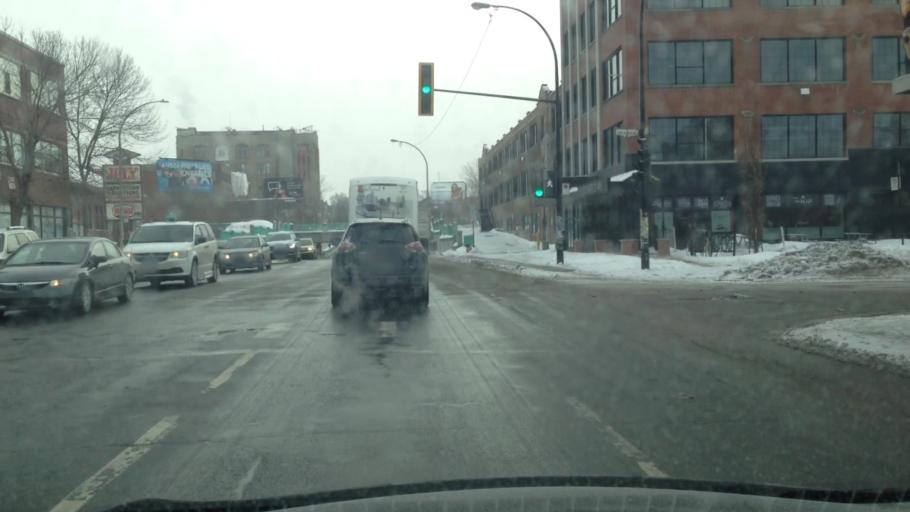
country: CA
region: Quebec
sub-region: Montreal
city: Montreal
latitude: 45.5270
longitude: -73.6131
